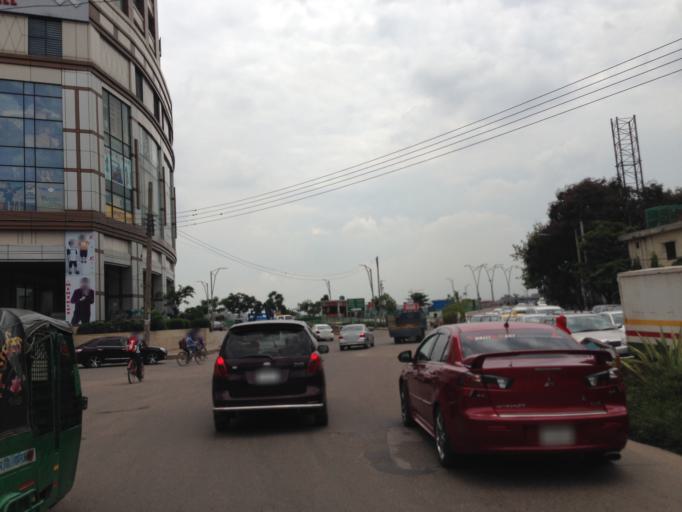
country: BD
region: Dhaka
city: Paltan
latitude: 23.7736
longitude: 90.4161
